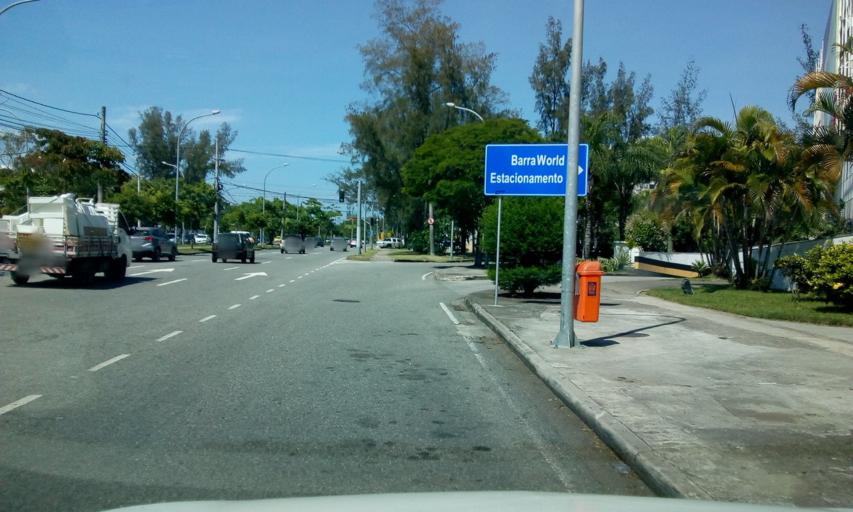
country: BR
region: Rio de Janeiro
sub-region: Nilopolis
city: Nilopolis
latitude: -23.0109
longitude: -43.4425
